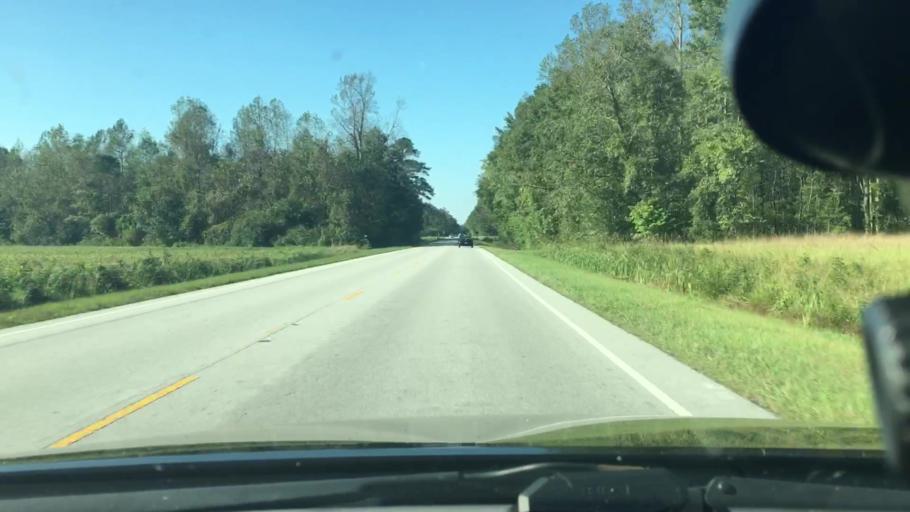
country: US
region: North Carolina
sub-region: Craven County
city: Vanceboro
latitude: 35.3059
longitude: -77.1355
